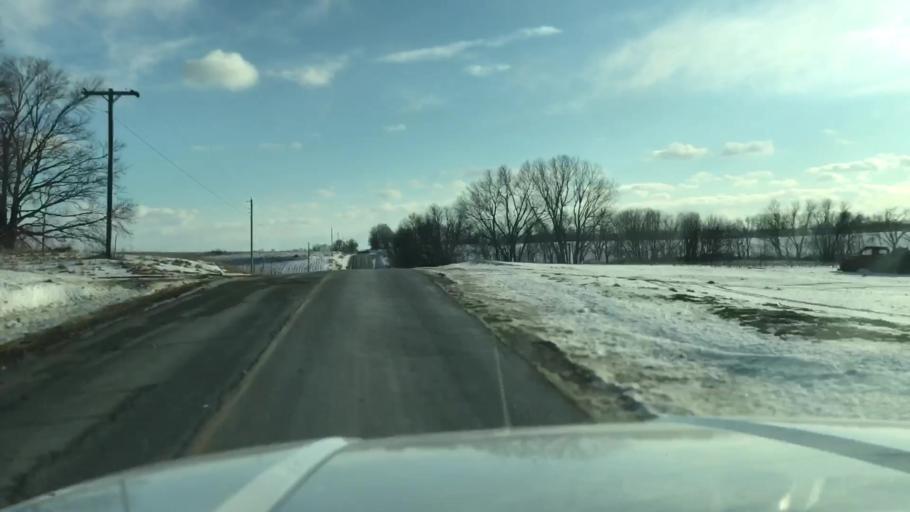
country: US
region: Missouri
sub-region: Holt County
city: Oregon
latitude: 40.0556
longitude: -94.9749
